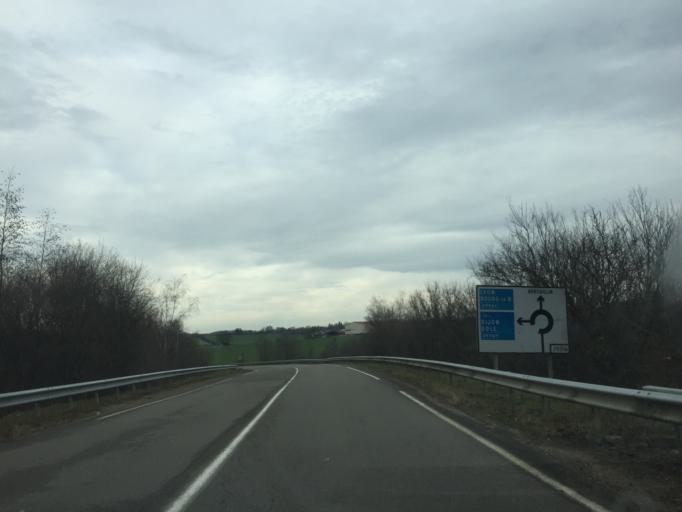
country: FR
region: Franche-Comte
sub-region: Departement du Jura
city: Poligny
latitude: 46.8474
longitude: 5.5770
